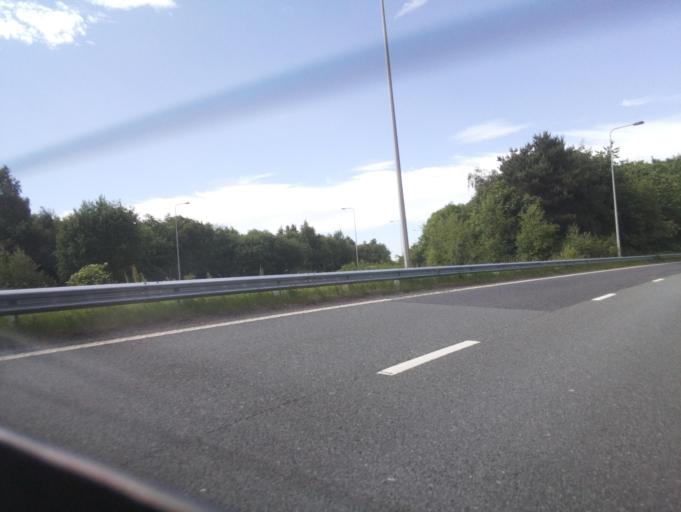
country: GB
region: England
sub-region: Warrington
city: Croft
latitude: 53.4243
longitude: -2.5478
